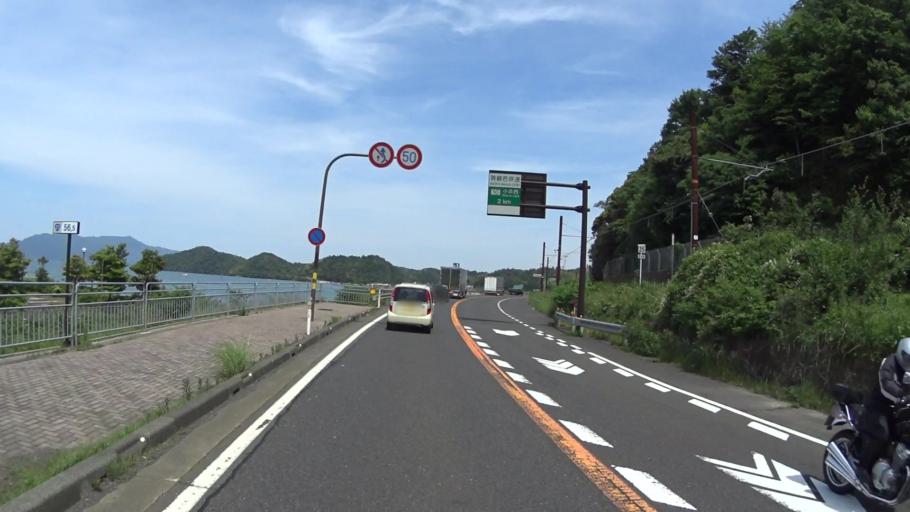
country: JP
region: Fukui
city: Obama
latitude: 35.4778
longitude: 135.6431
